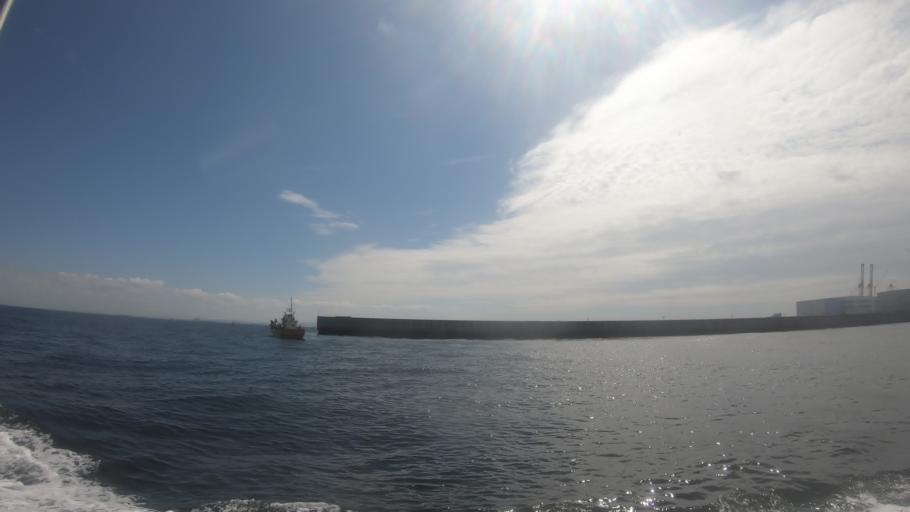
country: JP
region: Kanagawa
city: Yokohama
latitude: 35.4135
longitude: 139.6874
